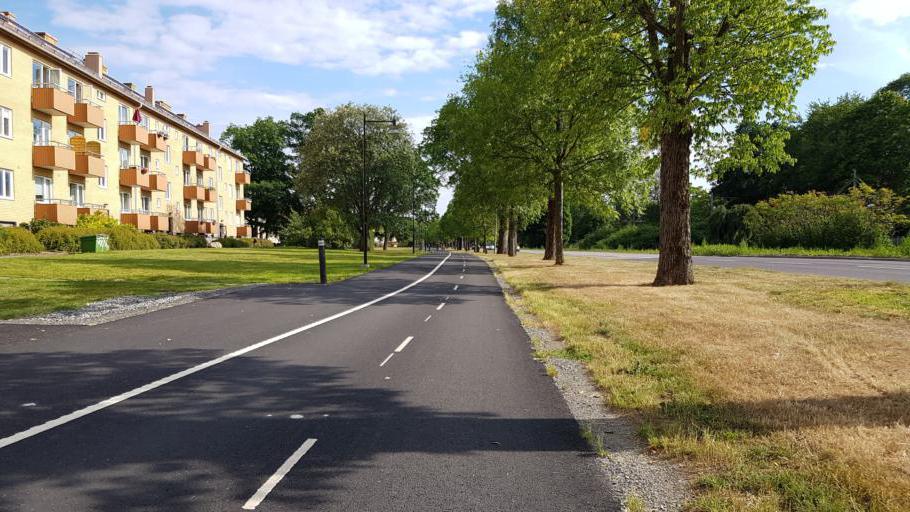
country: SE
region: Vaestra Goetaland
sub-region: Molndal
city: Moelndal
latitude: 57.7098
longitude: 12.0240
